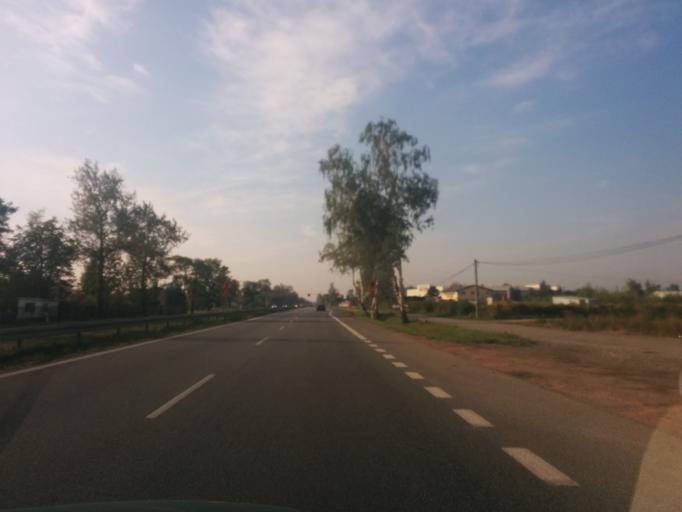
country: PL
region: Masovian Voivodeship
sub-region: Powiat pruszkowski
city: Nadarzyn
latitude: 52.0495
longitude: 20.8653
